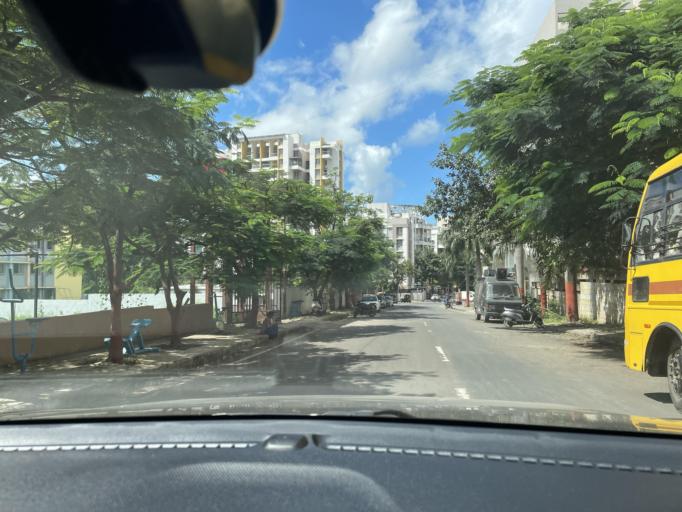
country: IN
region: Maharashtra
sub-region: Pune Division
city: Kharakvasla
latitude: 18.5101
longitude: 73.7773
